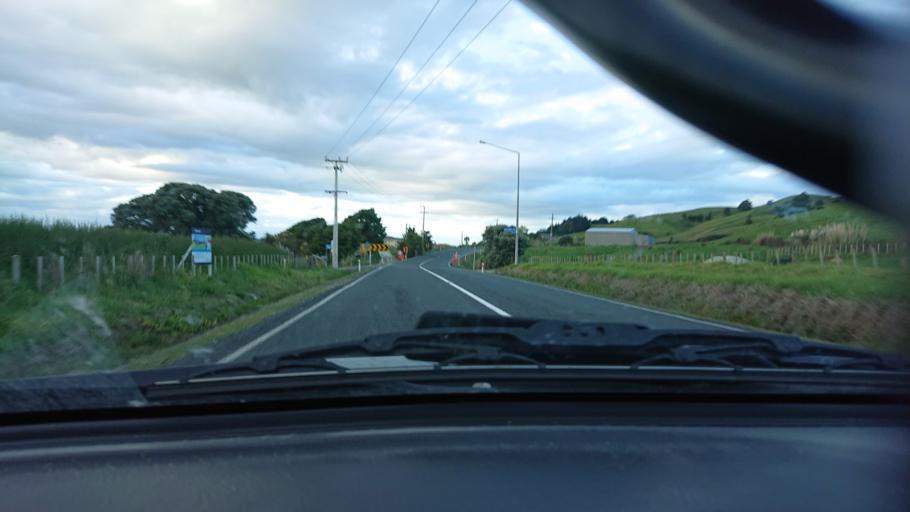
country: NZ
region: Auckland
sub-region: Auckland
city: Wellsford
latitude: -36.4506
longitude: 174.4337
